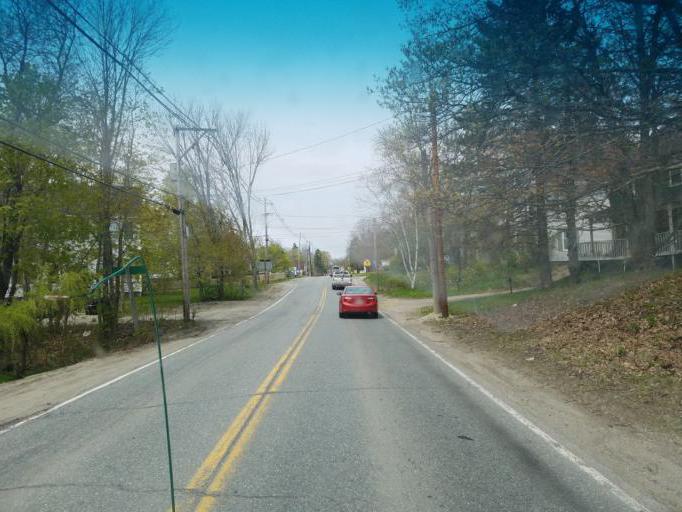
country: US
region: Maine
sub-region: Hancock County
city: Ellsworth
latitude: 44.5463
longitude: -68.4227
